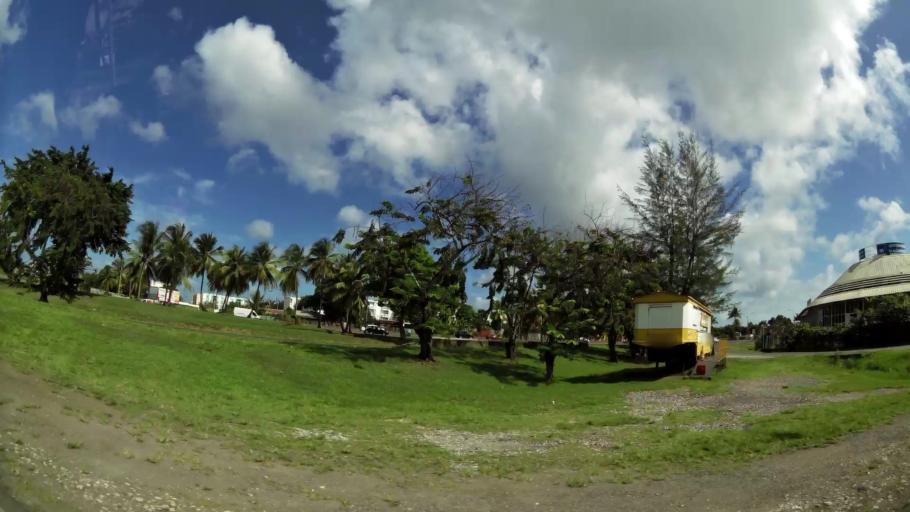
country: GP
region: Guadeloupe
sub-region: Guadeloupe
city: Pointe-a-Pitre
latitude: 16.2520
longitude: -61.5332
